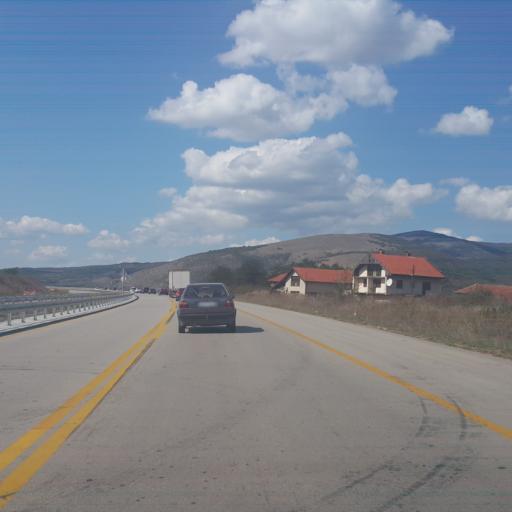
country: RS
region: Central Serbia
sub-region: Pirotski Okrug
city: Bela Palanka
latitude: 43.2223
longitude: 22.4062
